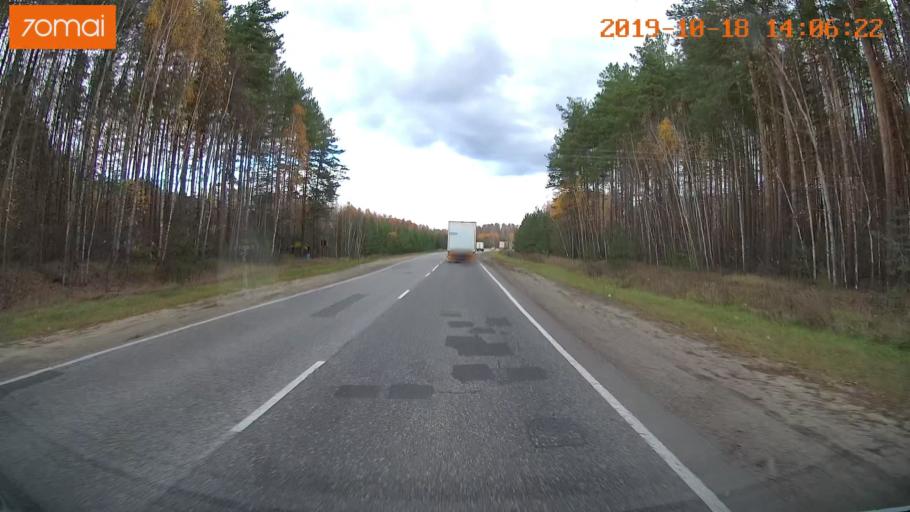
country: RU
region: Rjazan
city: Spas-Klepiki
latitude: 55.1444
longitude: 40.1498
